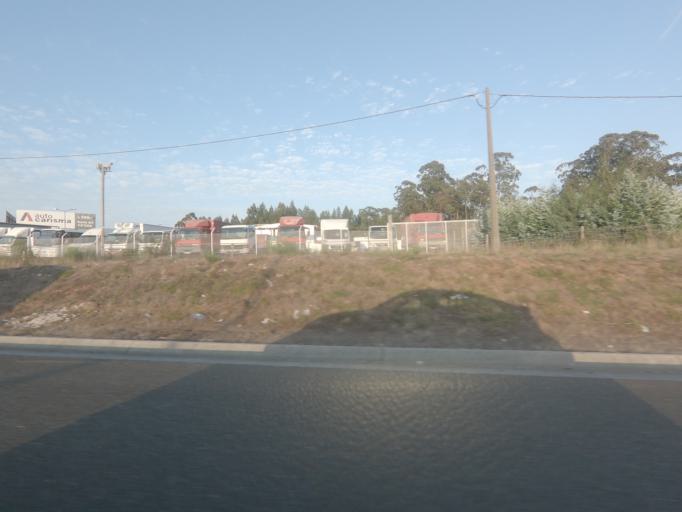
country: PT
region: Leiria
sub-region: Leiria
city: Santa Catarina da Serra
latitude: 39.6351
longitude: -8.6986
